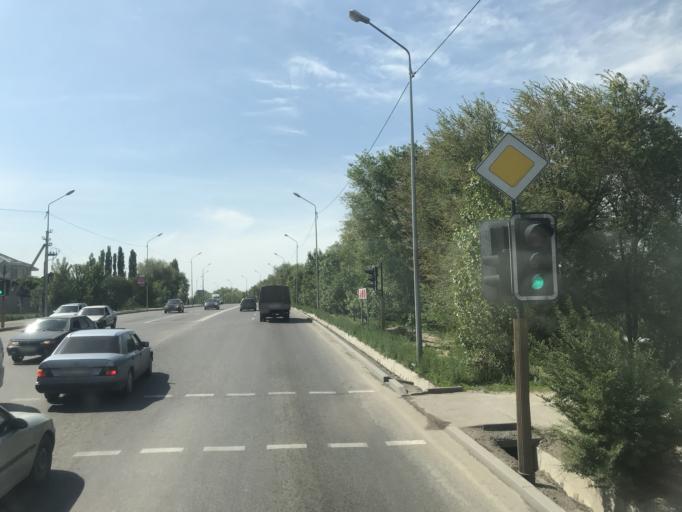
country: KZ
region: Almaty Oblysy
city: Burunday
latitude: 43.3111
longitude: 76.8667
